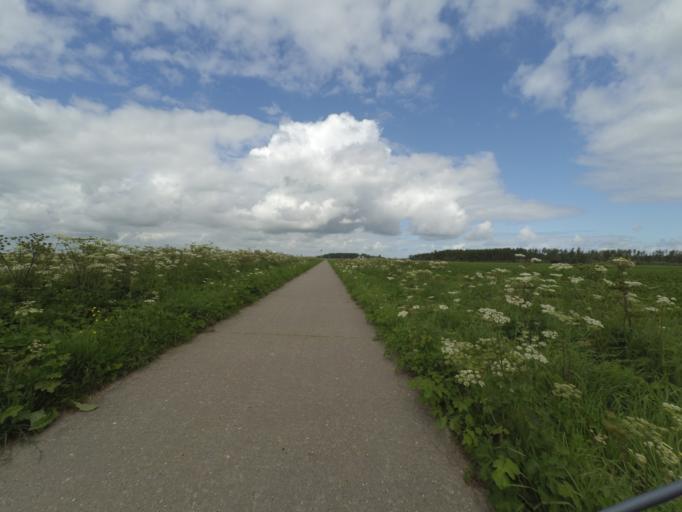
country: NL
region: Groningen
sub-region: Gemeente Zuidhorn
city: Grijpskerk
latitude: 53.3169
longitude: 6.2575
